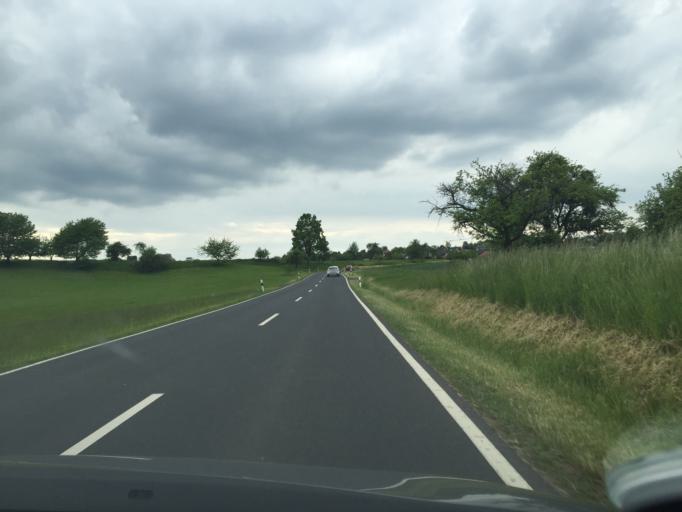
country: DE
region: Bavaria
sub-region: Regierungsbezirk Unterfranken
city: Goldbach
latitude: 50.0300
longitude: 9.1758
